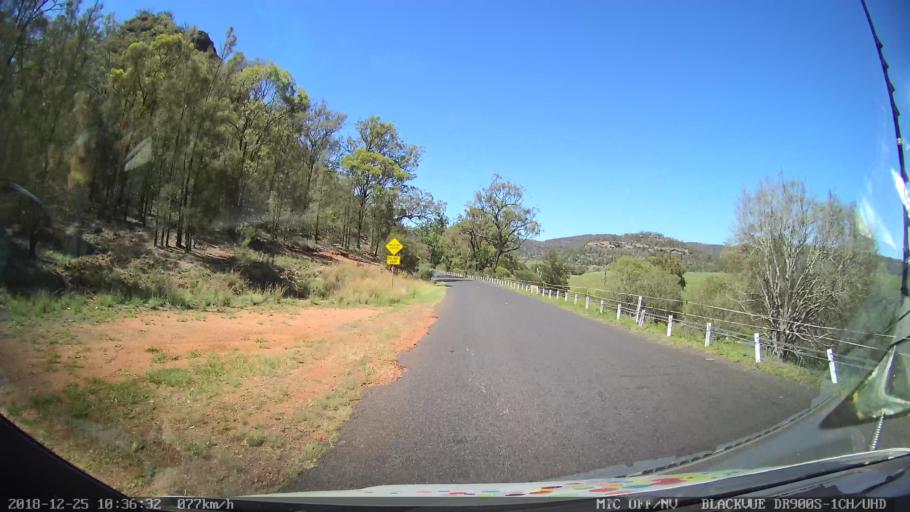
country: AU
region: New South Wales
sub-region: Upper Hunter Shire
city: Merriwa
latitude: -32.4047
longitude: 150.3846
